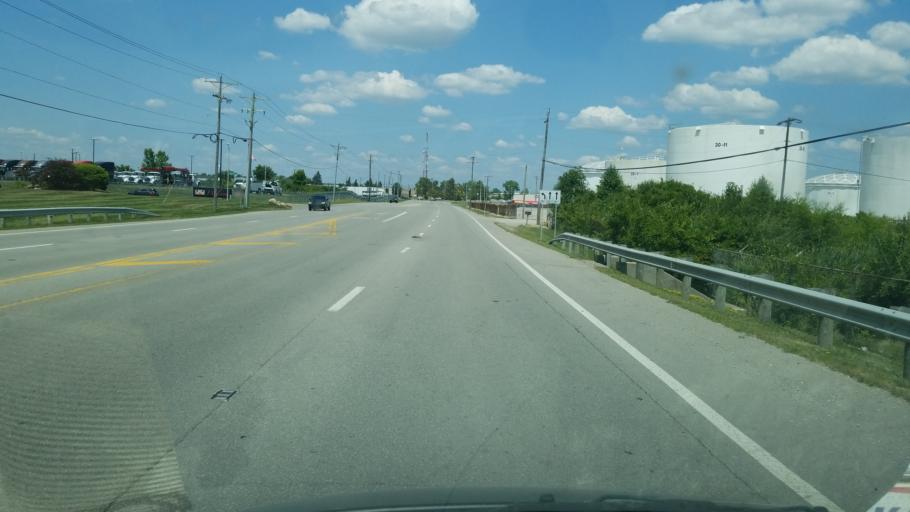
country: US
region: Ohio
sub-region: Franklin County
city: Lincoln Village
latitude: 39.9657
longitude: -83.1113
